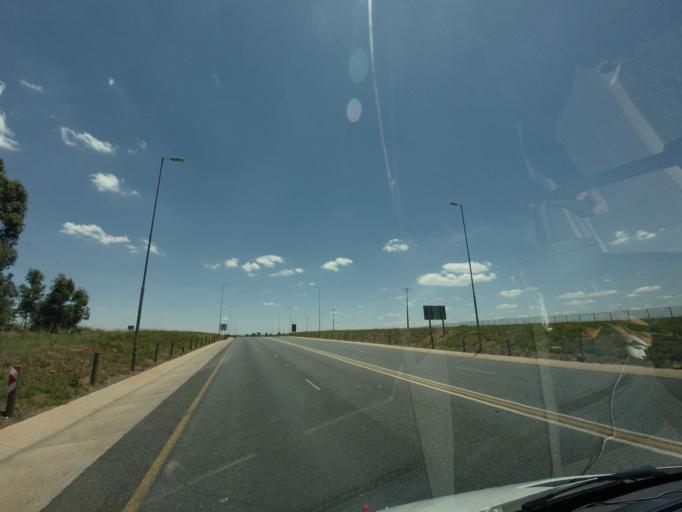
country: ZA
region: Mpumalanga
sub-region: Nkangala District Municipality
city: Belfast
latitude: -25.7281
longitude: 30.1372
